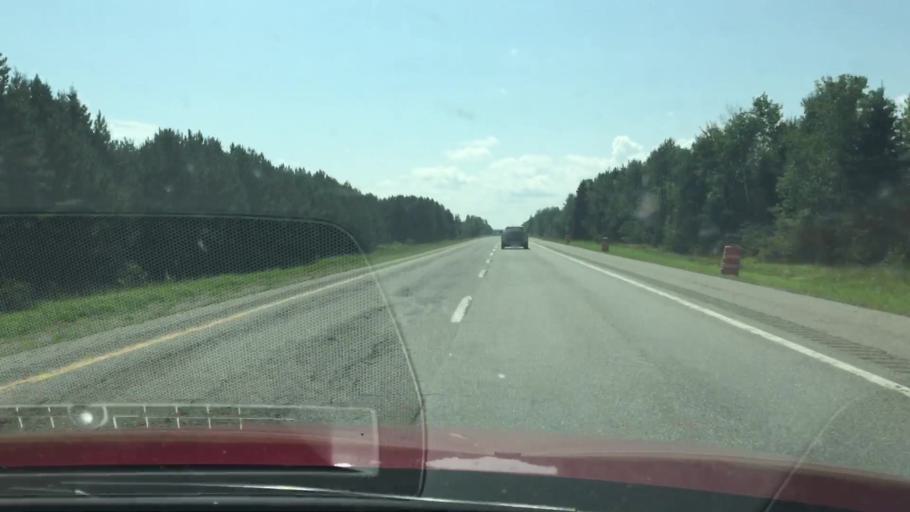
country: US
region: Maine
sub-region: Penobscot County
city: Patten
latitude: 45.8640
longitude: -68.4190
